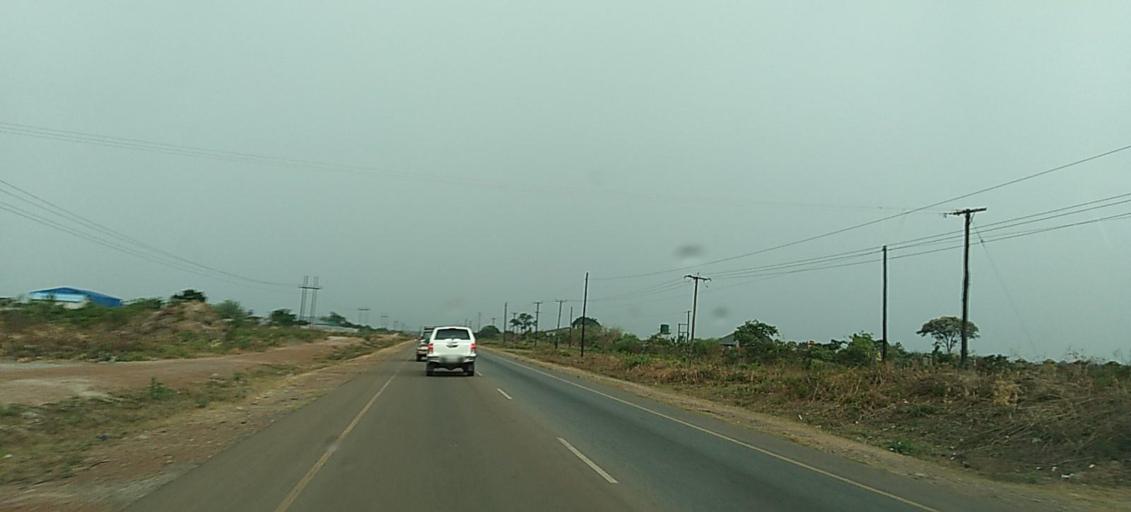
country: ZM
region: Copperbelt
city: Kalulushi
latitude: -12.8351
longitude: 28.1215
